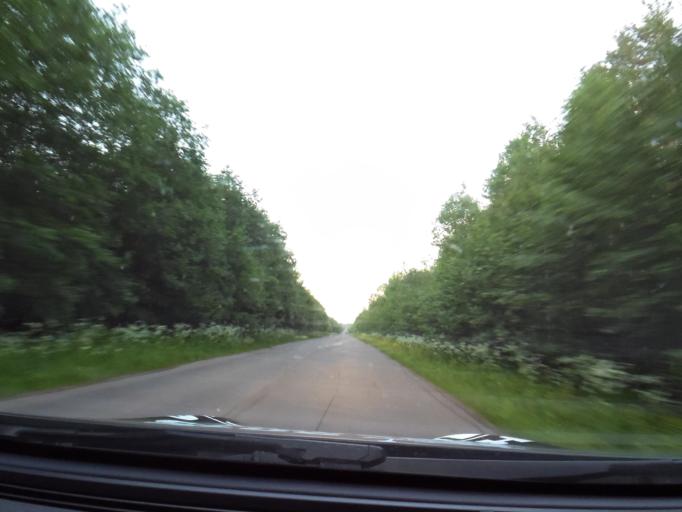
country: RU
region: Leningrad
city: Voznesen'ye
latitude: 60.8291
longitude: 35.7025
